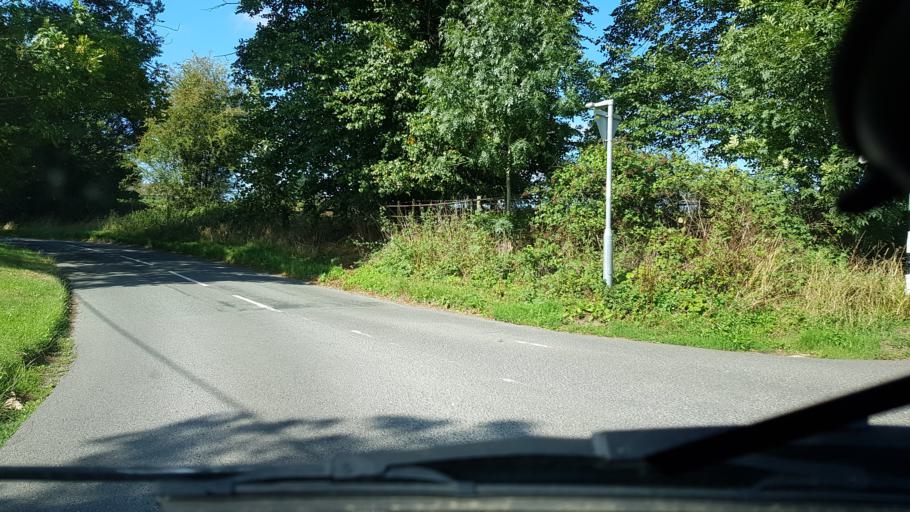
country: GB
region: England
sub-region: West Sussex
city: Horsham
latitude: 51.0929
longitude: -0.3459
